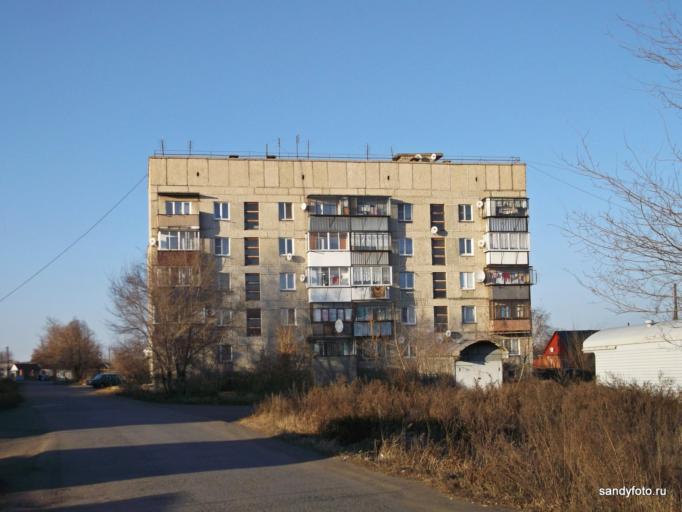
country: RU
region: Chelyabinsk
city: Troitsk
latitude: 54.1081
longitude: 61.5807
